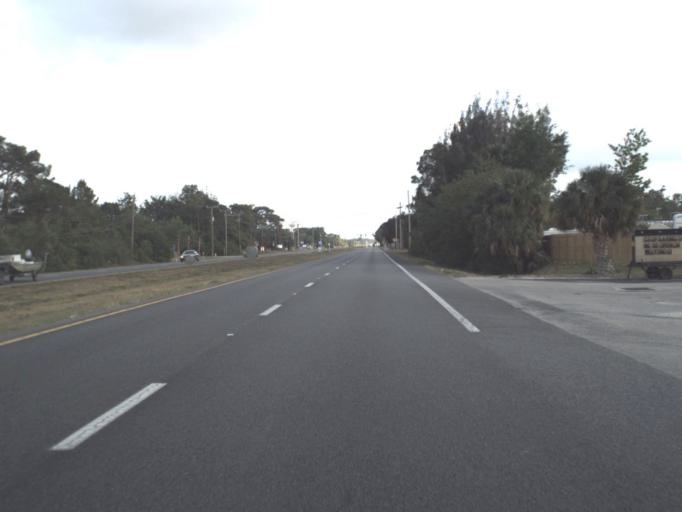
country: US
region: Florida
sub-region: Brevard County
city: Mims
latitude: 28.6903
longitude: -80.8568
